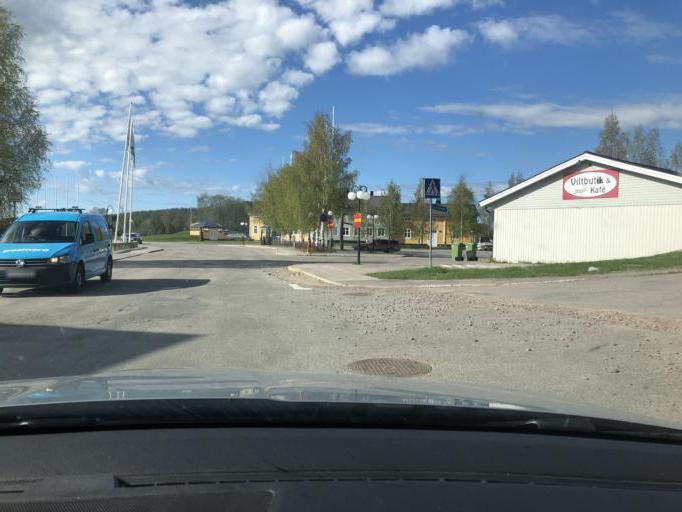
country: SE
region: Norrbotten
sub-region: Arjeplogs Kommun
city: Arjeplog
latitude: 66.0520
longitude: 17.8883
